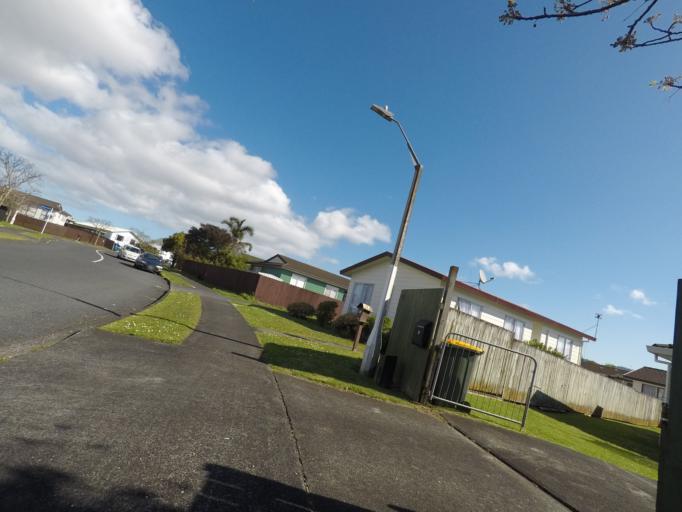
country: NZ
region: Auckland
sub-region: Auckland
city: Rosebank
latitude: -36.8606
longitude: 174.6019
